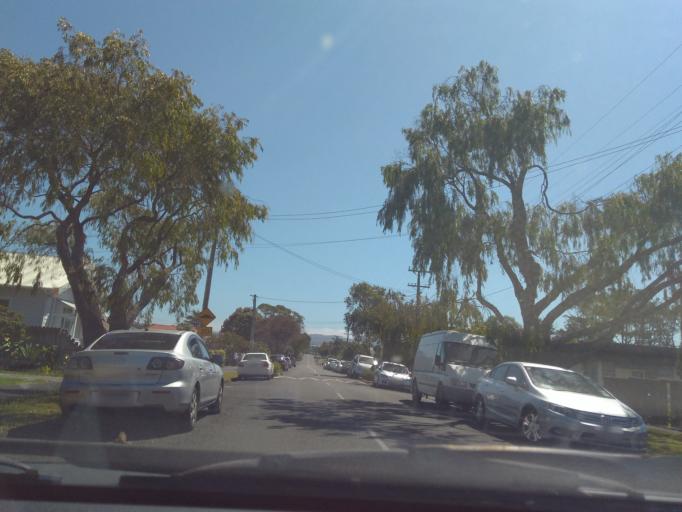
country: NZ
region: Auckland
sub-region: Auckland
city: Rosebank
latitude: -36.8989
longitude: 174.6953
